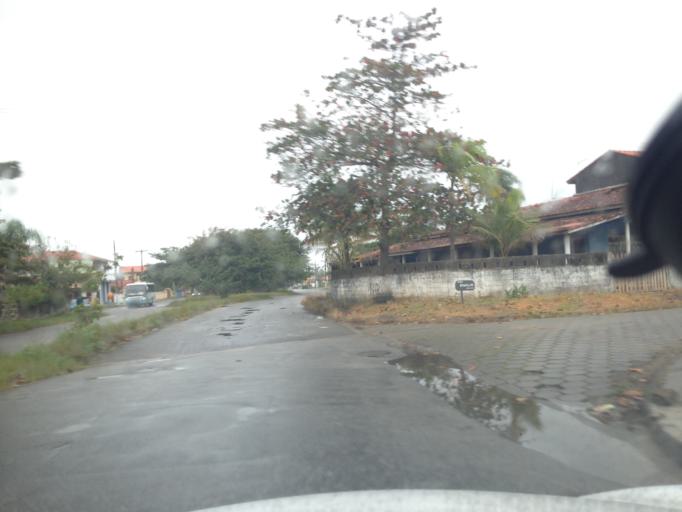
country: BR
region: Sao Paulo
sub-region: Itanhaem
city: Itanhaem
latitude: -24.2296
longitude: -46.8732
